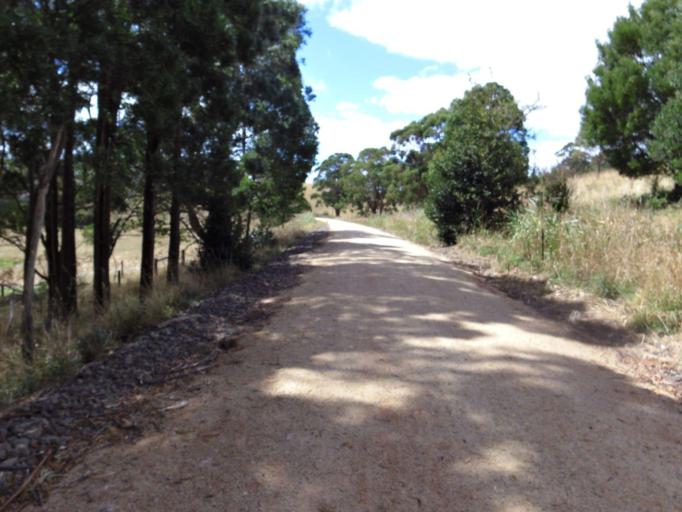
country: AU
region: Victoria
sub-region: Baw Baw
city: Warragul
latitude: -38.4293
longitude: 145.8542
